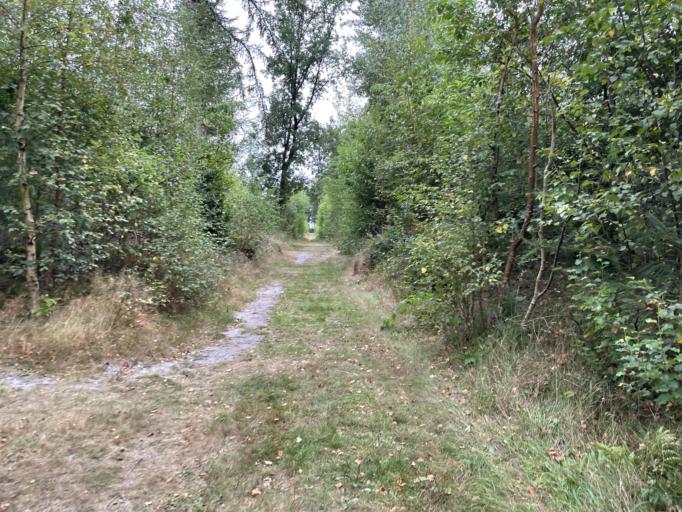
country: DE
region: Schleswig-Holstein
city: Mildstedt
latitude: 54.4708
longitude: 9.1119
